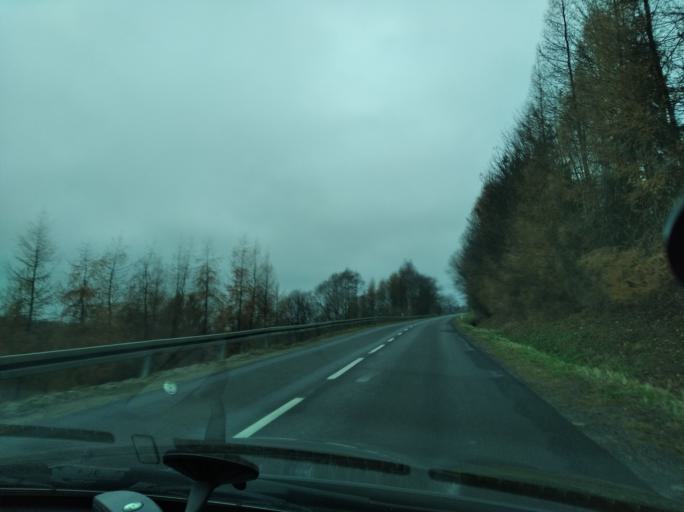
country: PL
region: Subcarpathian Voivodeship
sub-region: Powiat przeworski
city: Jawornik Polski
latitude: 49.8825
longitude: 22.2403
